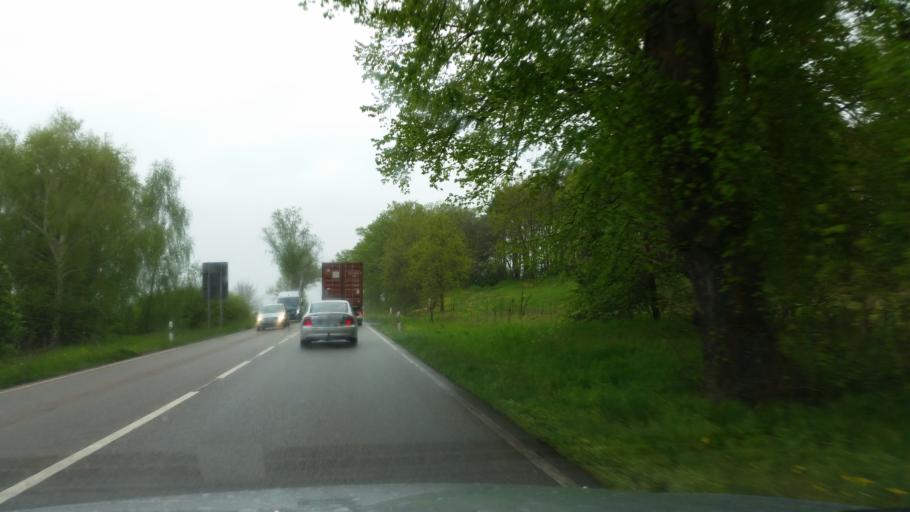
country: DE
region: Saxony-Anhalt
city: Kalbe
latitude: 52.6050
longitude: 11.3243
